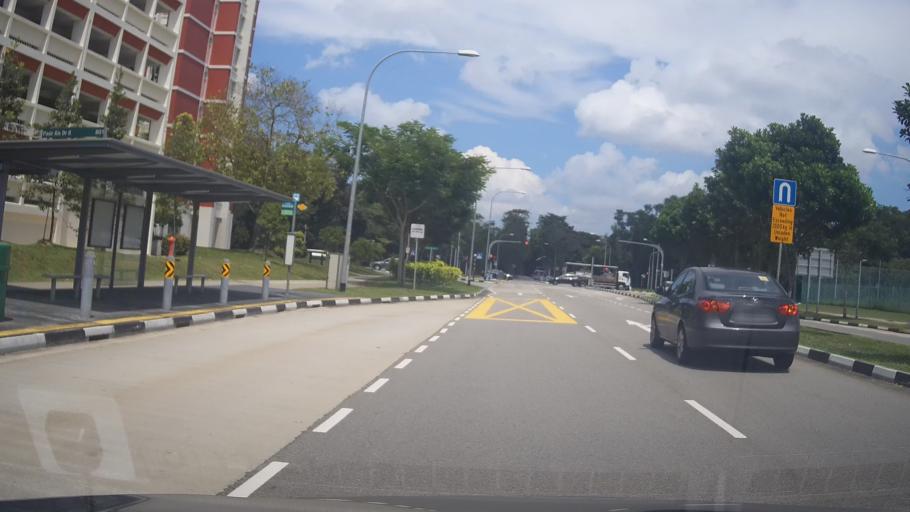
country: MY
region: Johor
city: Kampung Pasir Gudang Baru
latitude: 1.3741
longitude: 103.9482
